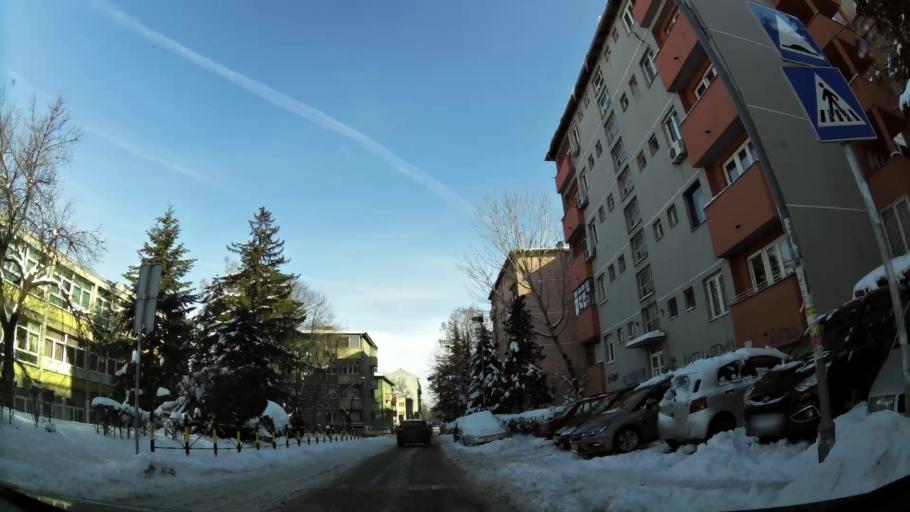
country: RS
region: Central Serbia
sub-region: Belgrade
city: Palilula
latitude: 44.8151
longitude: 20.5064
